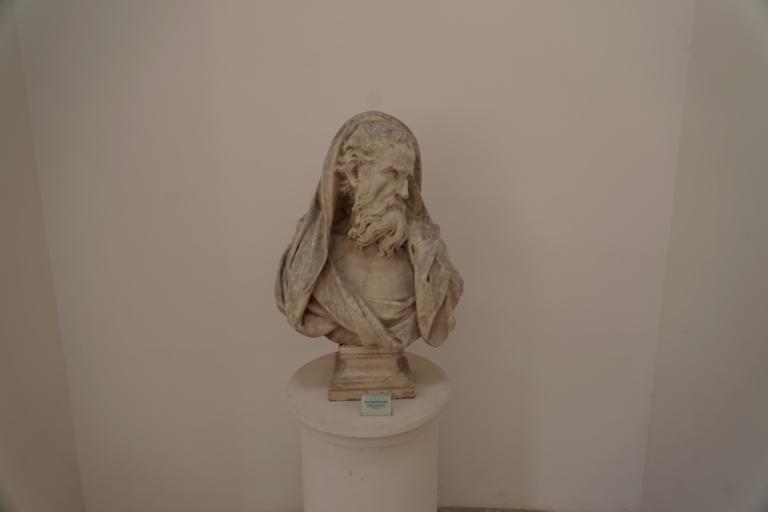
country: RU
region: St.-Petersburg
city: Tyarlevo
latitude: 59.6882
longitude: 30.4558
